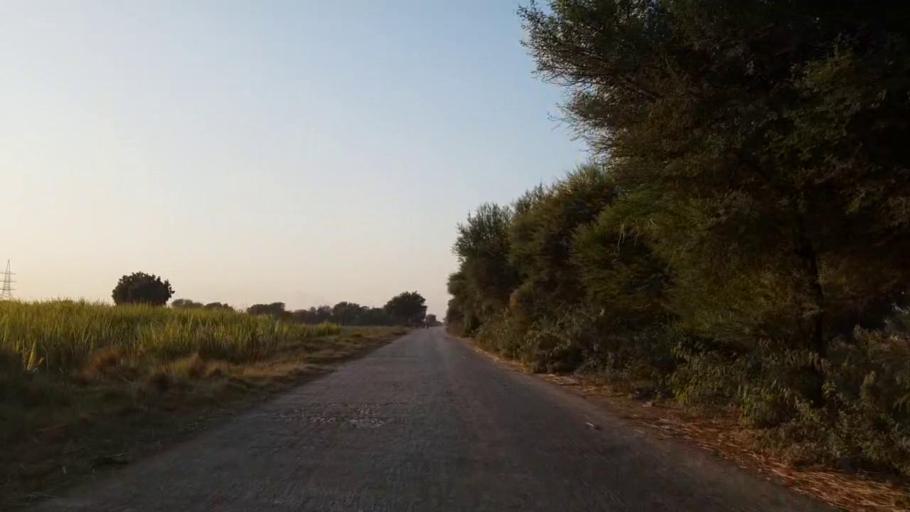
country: PK
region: Sindh
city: Chambar
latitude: 25.2387
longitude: 68.6944
